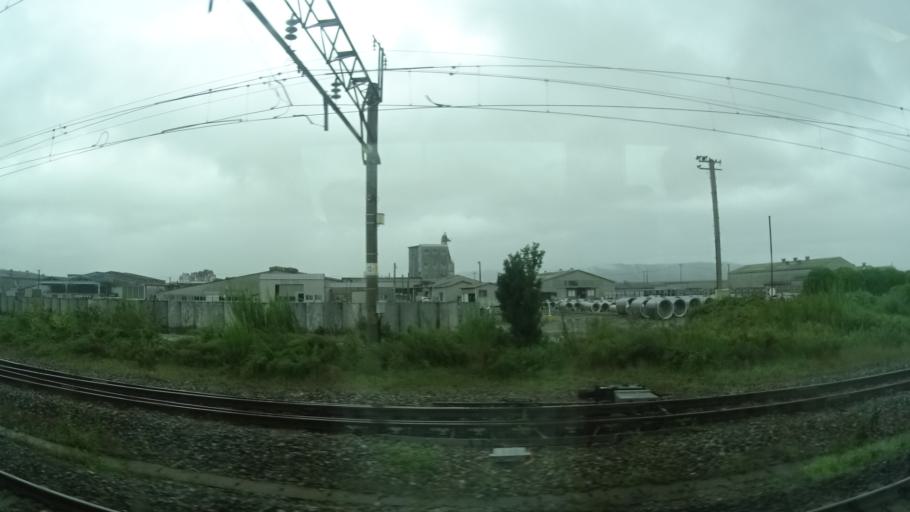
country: JP
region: Yamagata
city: Sakata
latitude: 38.8425
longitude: 139.9125
